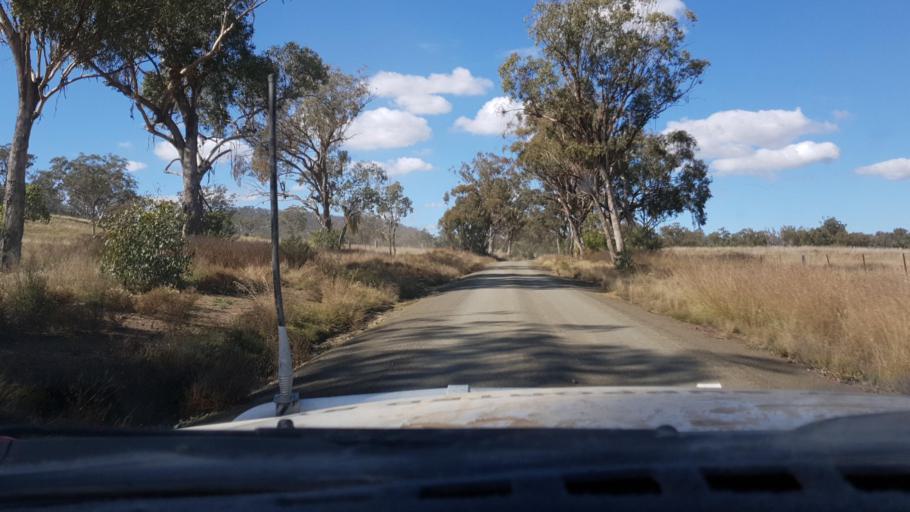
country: AU
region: New South Wales
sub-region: Tamworth Municipality
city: Manilla
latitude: -30.4706
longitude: 150.7521
